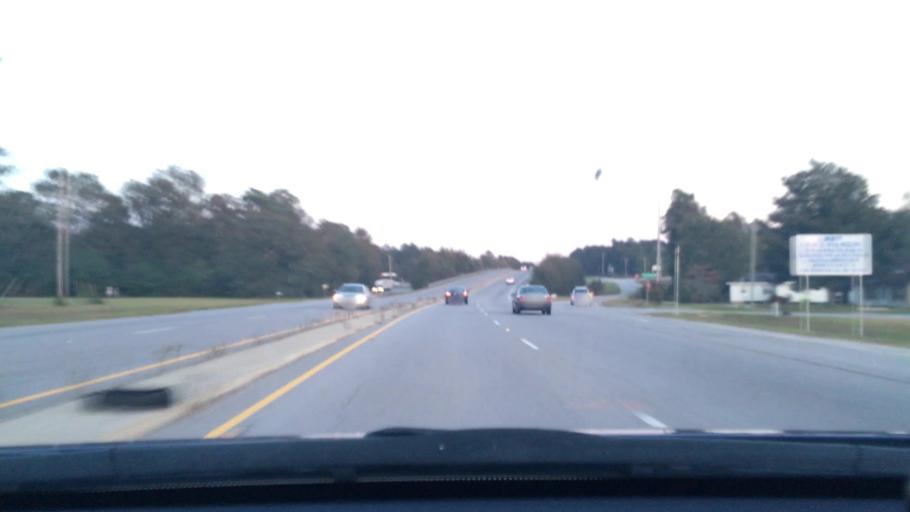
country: US
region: South Carolina
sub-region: Richland County
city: Gadsden
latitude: 33.9426
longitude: -80.6917
